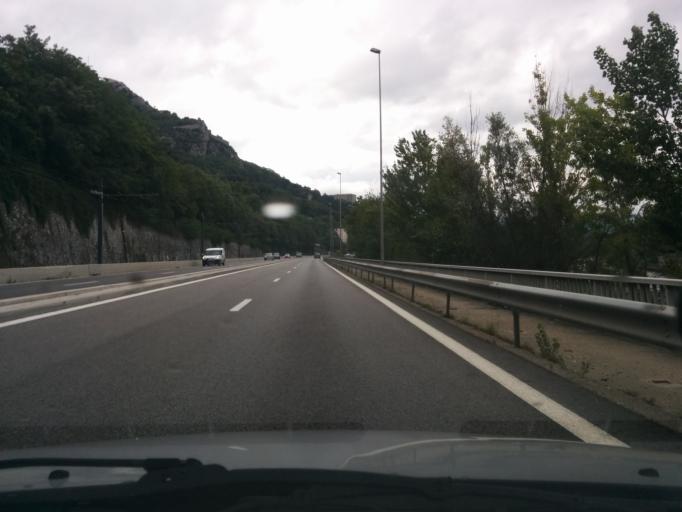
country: FR
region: Rhone-Alpes
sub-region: Departement de l'Isere
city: Saint-Martin-le-Vinoux
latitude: 45.2033
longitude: 5.7134
